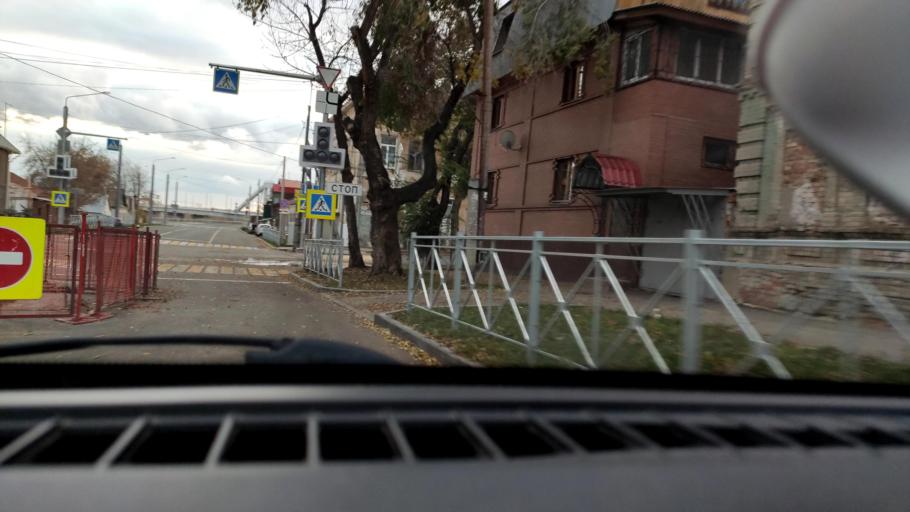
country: RU
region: Samara
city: Rozhdestveno
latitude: 53.1804
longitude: 50.0887
